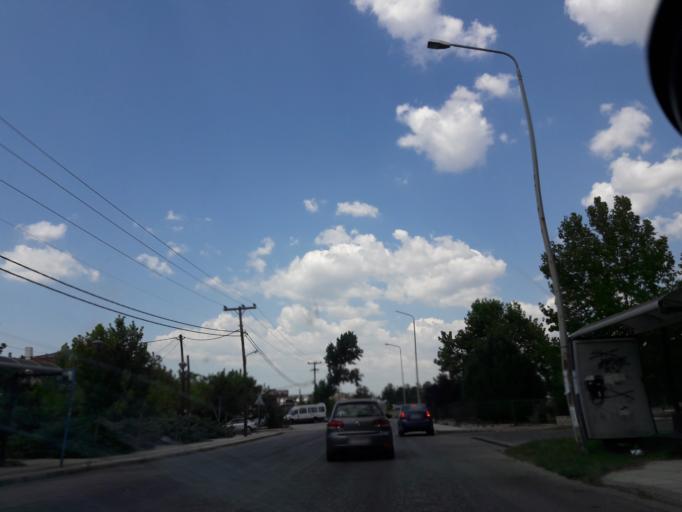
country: GR
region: Central Macedonia
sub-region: Nomos Thessalonikis
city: Thermi
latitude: 40.5258
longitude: 23.0484
